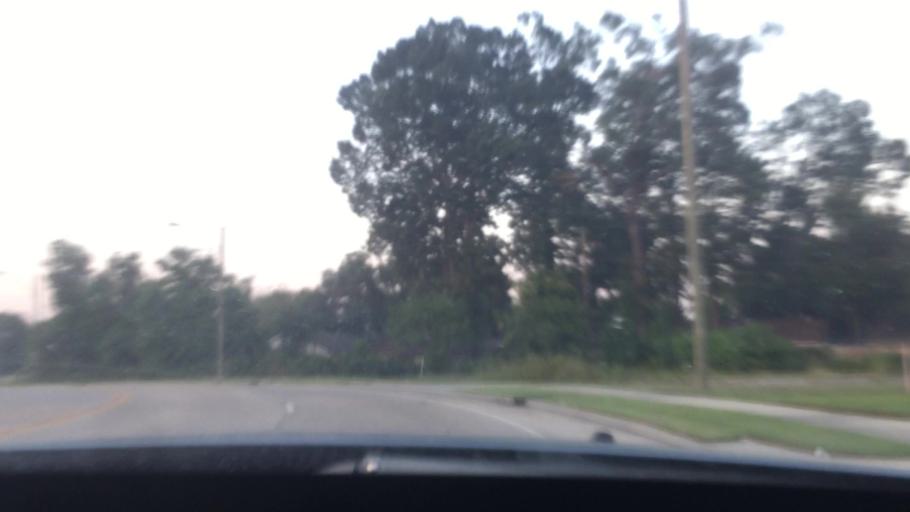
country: US
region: Louisiana
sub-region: East Baton Rouge Parish
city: Westminster
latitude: 30.4286
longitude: -91.0558
